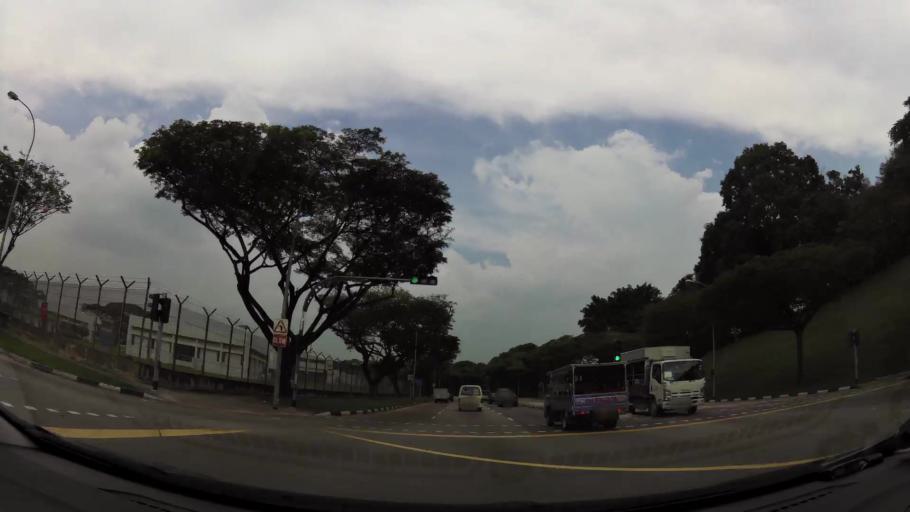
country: SG
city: Singapore
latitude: 1.3402
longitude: 103.9182
